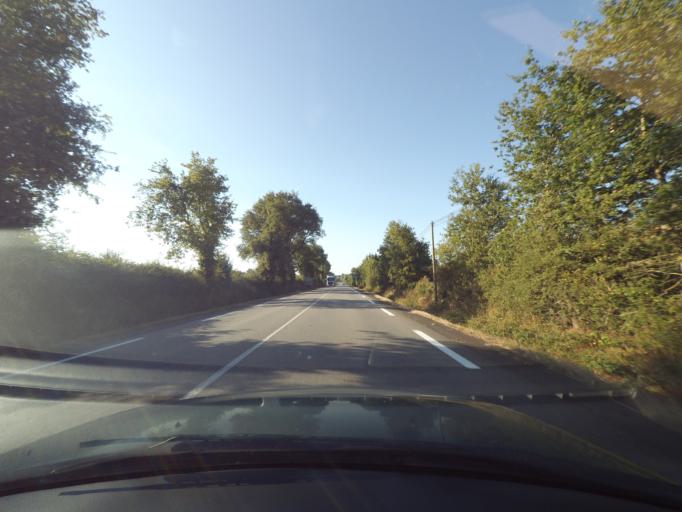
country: FR
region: Poitou-Charentes
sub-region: Departement des Deux-Sevres
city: Chiche
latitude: 46.7506
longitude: -0.3073
